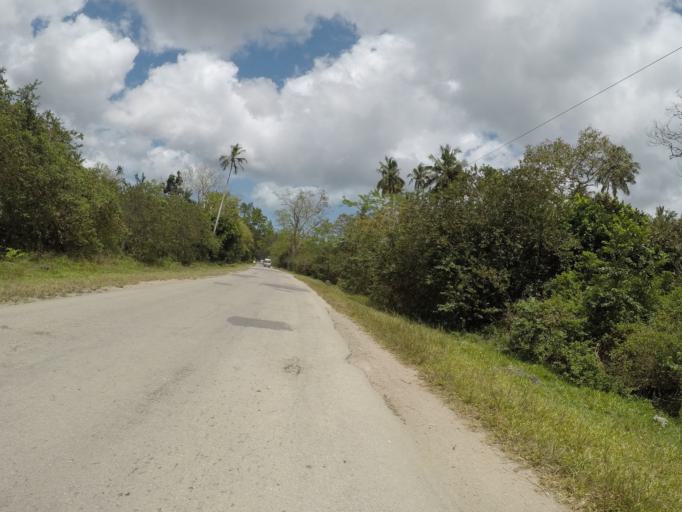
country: TZ
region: Zanzibar Central/South
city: Nganane
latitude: -6.2729
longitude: 39.4188
